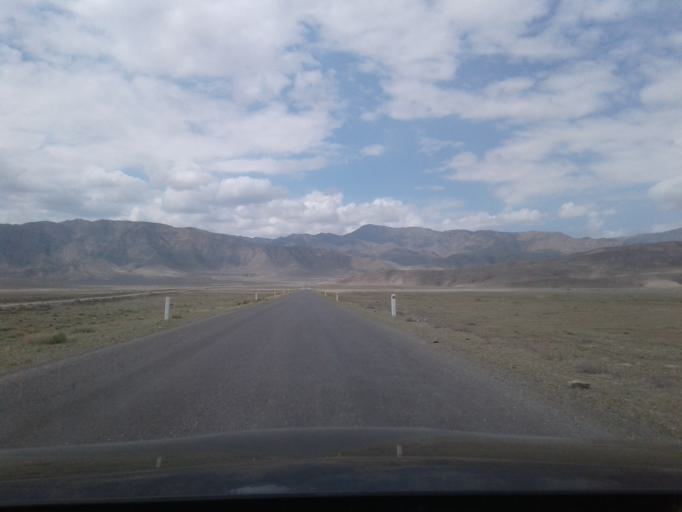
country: TM
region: Ahal
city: Baharly
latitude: 38.5265
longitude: 57.1451
